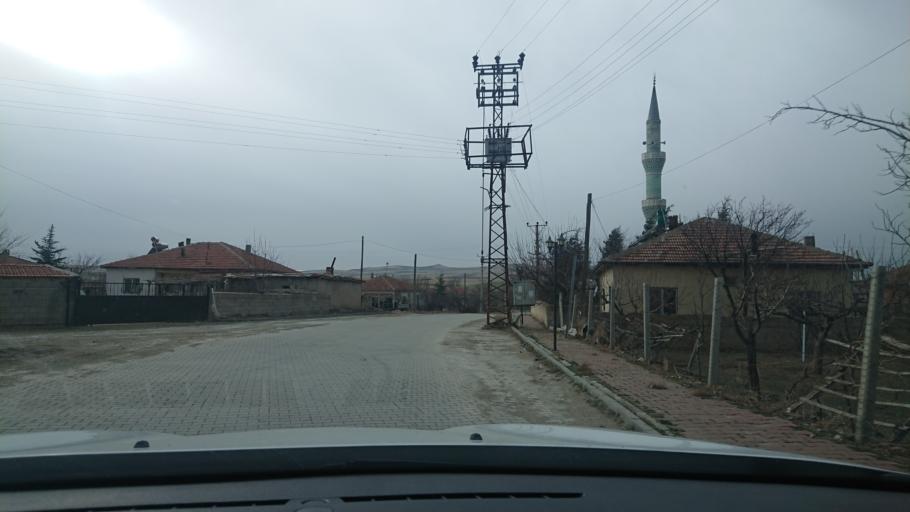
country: TR
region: Aksaray
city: Agacoren
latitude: 38.9261
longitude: 33.9540
